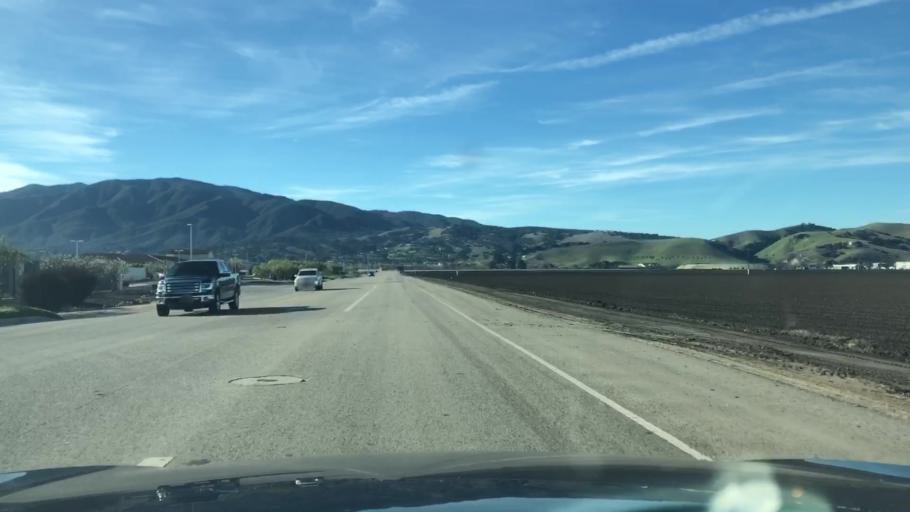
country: US
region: California
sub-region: Monterey County
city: Salinas
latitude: 36.6247
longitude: -121.6302
